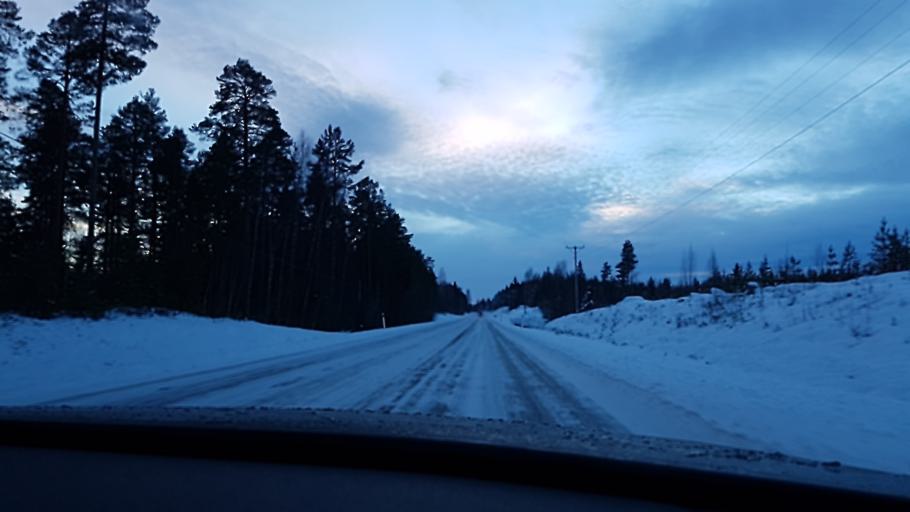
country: SE
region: Jaemtland
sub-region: Harjedalens Kommun
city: Sveg
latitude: 62.0857
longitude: 14.9509
